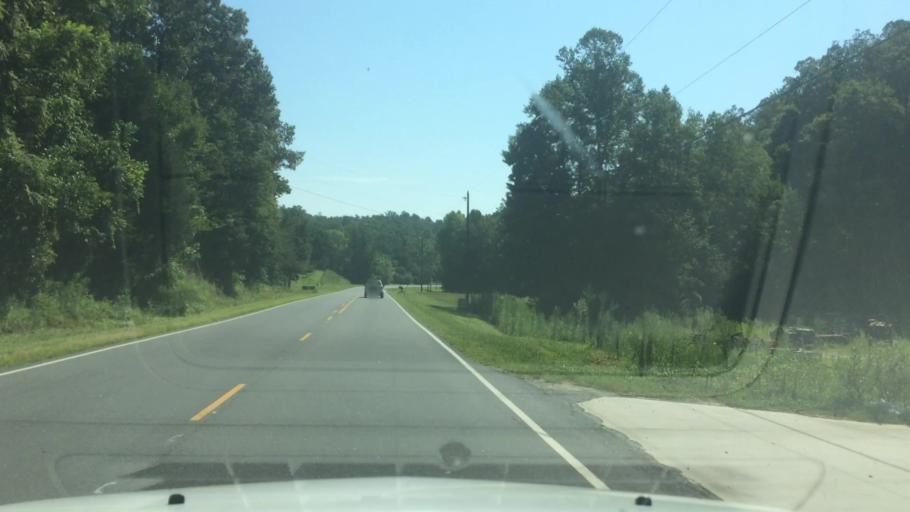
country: US
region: North Carolina
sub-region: Caldwell County
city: Lenoir
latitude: 35.9169
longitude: -81.4645
